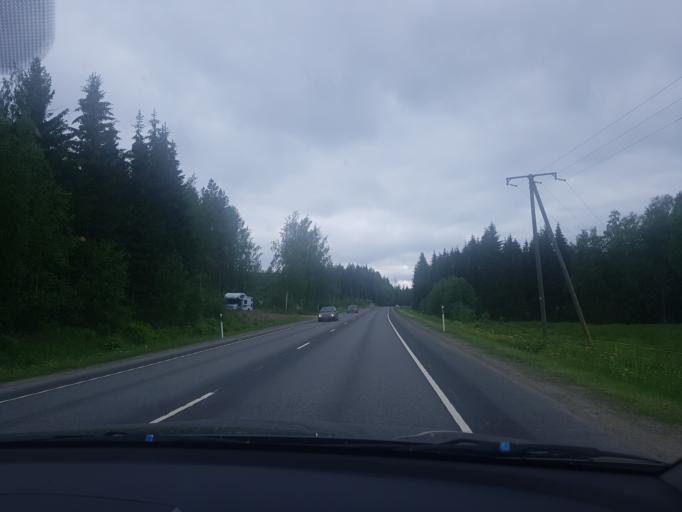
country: FI
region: Pirkanmaa
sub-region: Tampere
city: Paelkaene
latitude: 61.4026
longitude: 24.1897
